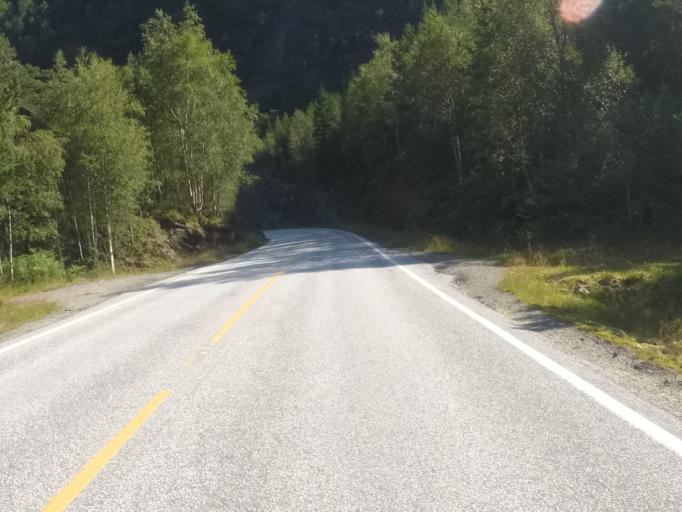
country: NO
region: Sogn og Fjordane
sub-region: Bremanger
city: Svelgen
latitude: 61.6185
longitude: 5.3134
